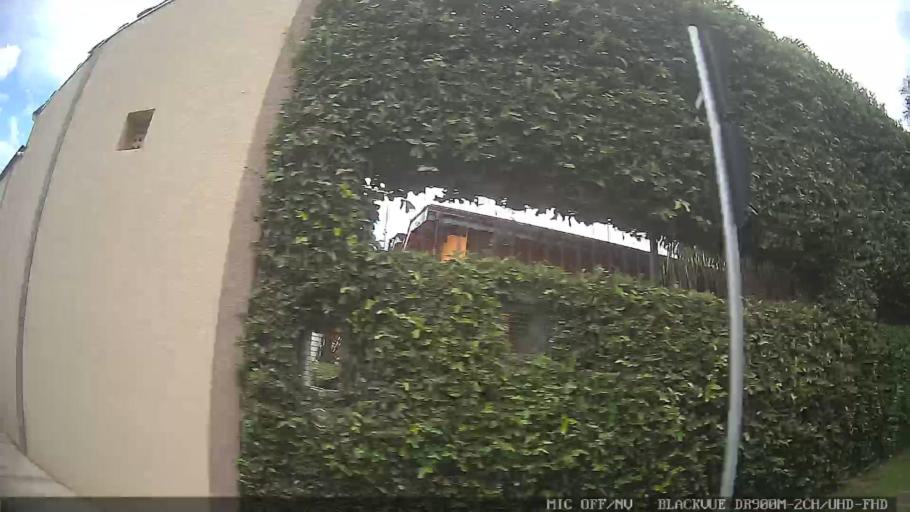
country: BR
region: Sao Paulo
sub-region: Atibaia
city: Atibaia
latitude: -23.1410
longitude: -46.5621
